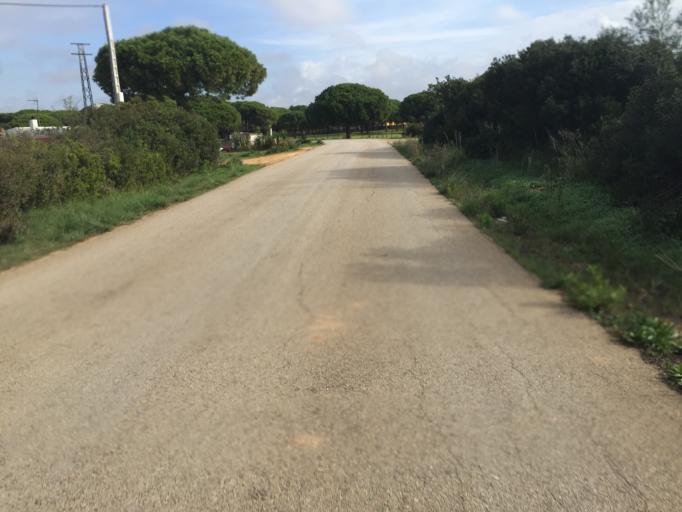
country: ES
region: Andalusia
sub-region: Provincia de Cadiz
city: Conil de la Frontera
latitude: 36.3094
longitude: -6.1173
